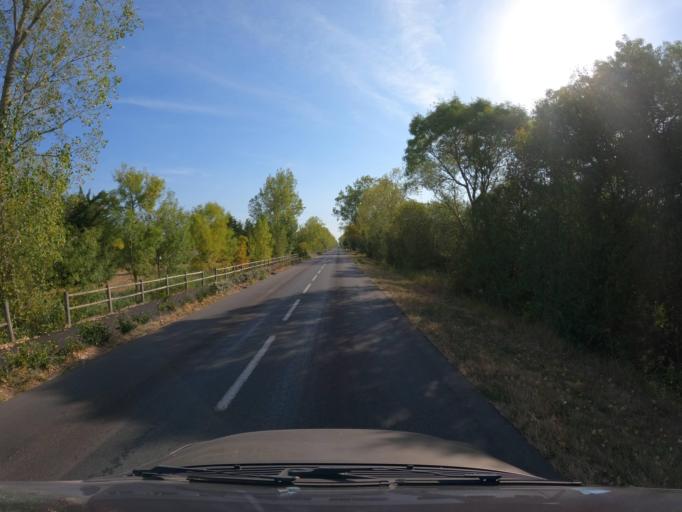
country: FR
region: Pays de la Loire
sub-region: Departement de la Vendee
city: Saint-Jean-de-Monts
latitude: 46.7993
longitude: -2.0400
